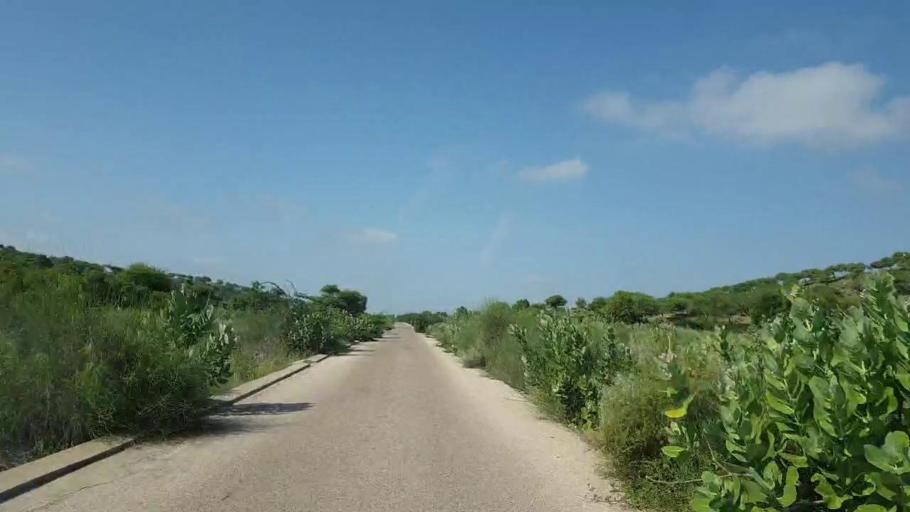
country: PK
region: Sindh
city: Mithi
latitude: 24.5494
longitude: 69.8837
